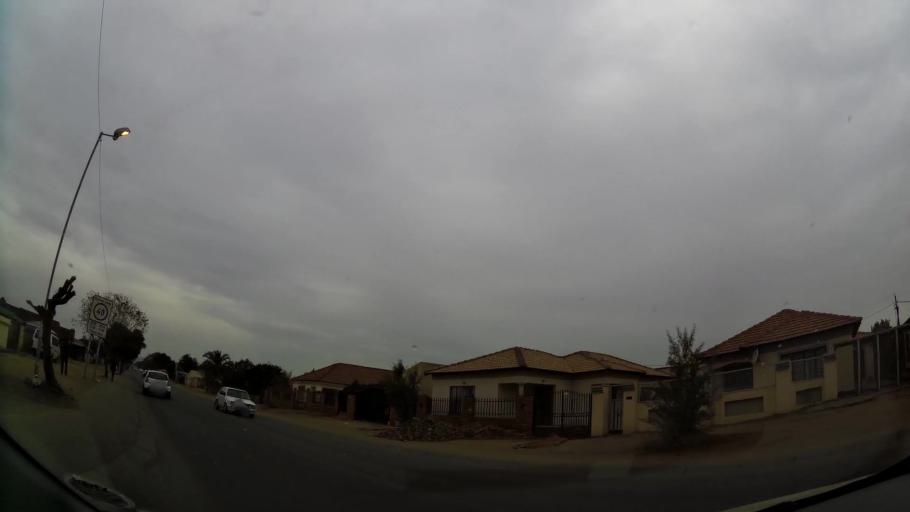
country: ZA
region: Gauteng
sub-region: City of Tshwane Metropolitan Municipality
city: Pretoria
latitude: -25.7147
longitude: 28.3422
